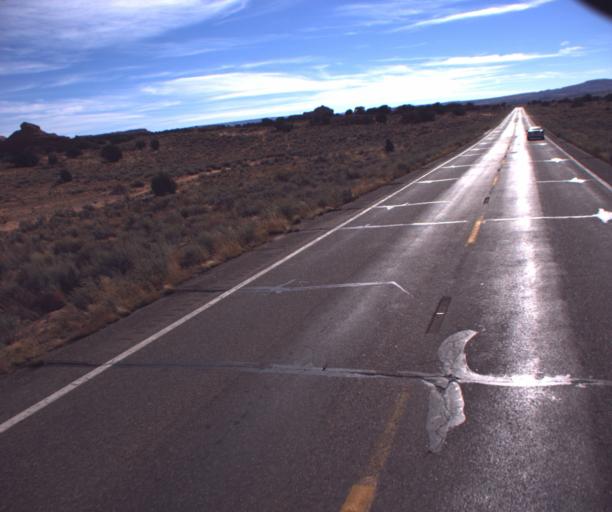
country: US
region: Arizona
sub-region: Coconino County
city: Kaibito
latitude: 36.6357
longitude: -111.2127
